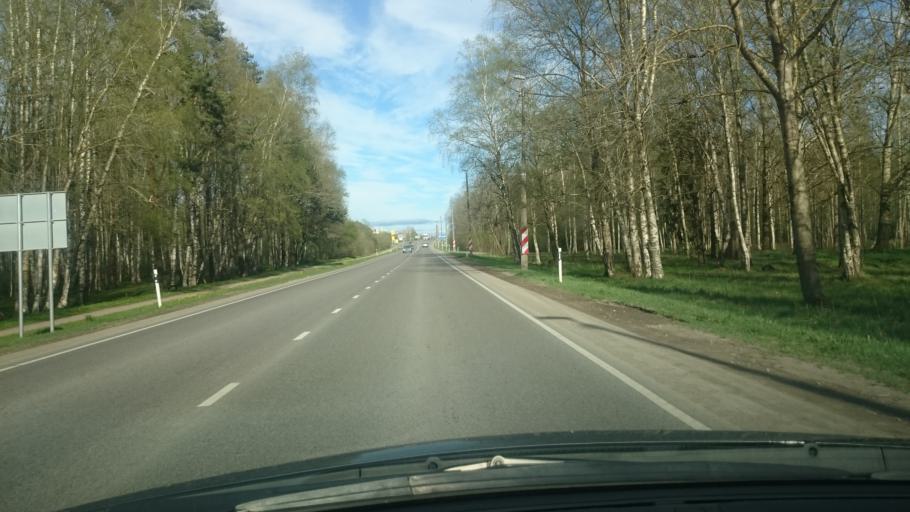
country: EE
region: Ida-Virumaa
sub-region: Sillamaee linn
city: Sillamae
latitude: 59.3908
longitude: 27.7666
